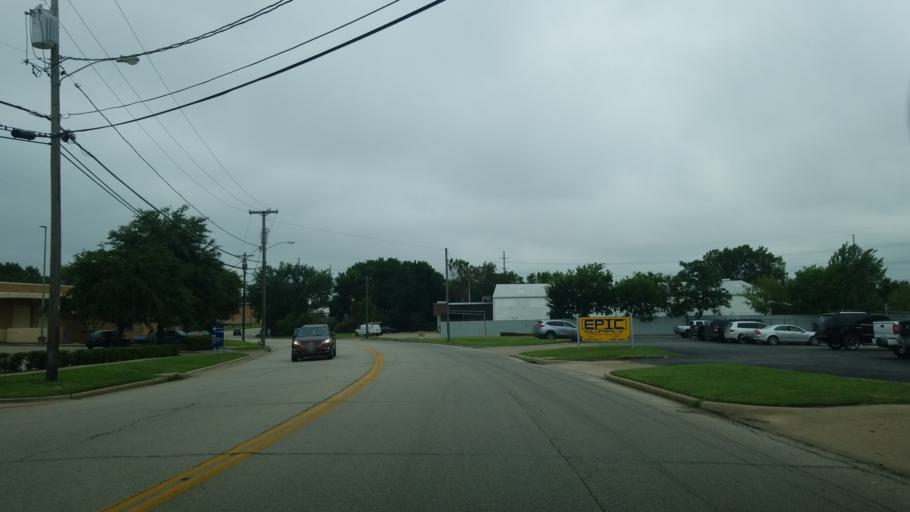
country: US
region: Texas
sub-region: Dallas County
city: University Park
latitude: 32.8447
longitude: -96.8695
